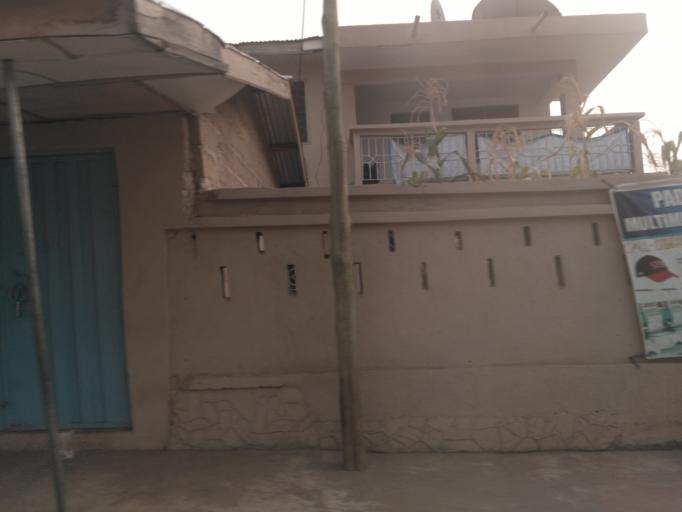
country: GH
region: Ashanti
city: Kumasi
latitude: 6.7094
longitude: -1.6126
